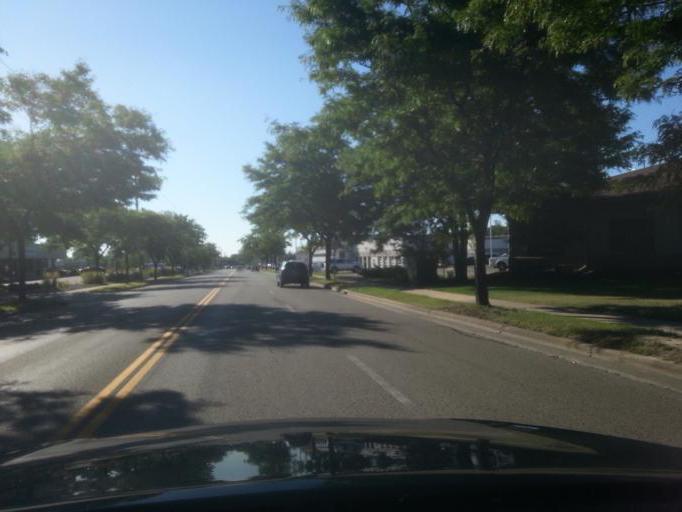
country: US
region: Wisconsin
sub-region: Dane County
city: Shorewood Hills
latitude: 43.0530
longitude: -89.4849
